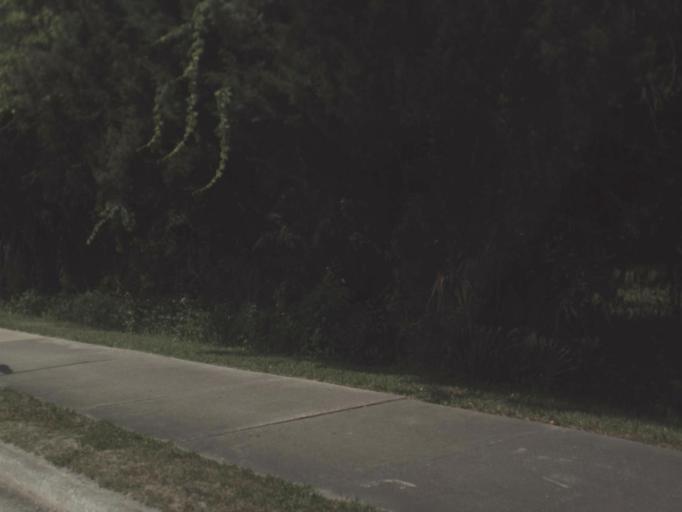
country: US
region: Florida
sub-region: Duval County
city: Atlantic Beach
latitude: 30.3436
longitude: -81.4133
